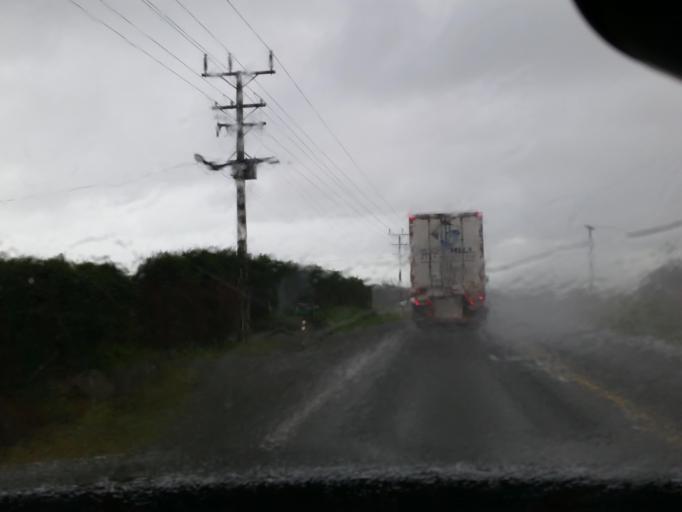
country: NZ
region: Southland
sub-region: Invercargill City
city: Bluff
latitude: -46.5432
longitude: 168.3014
